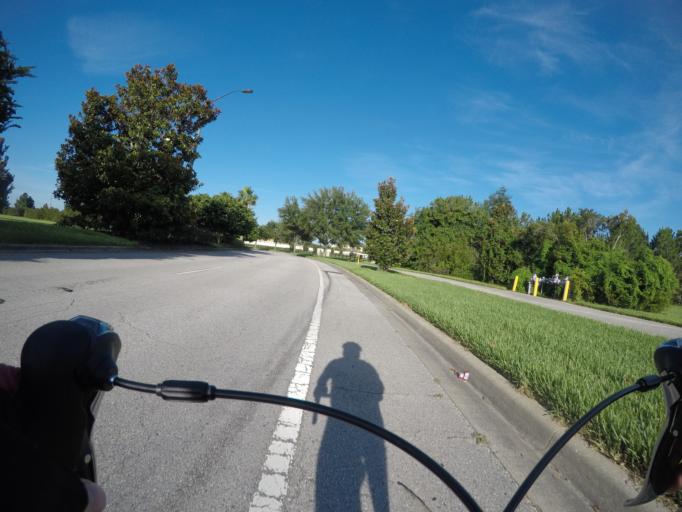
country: US
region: Florida
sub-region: Orange County
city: Taft
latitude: 28.4048
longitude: -81.2457
